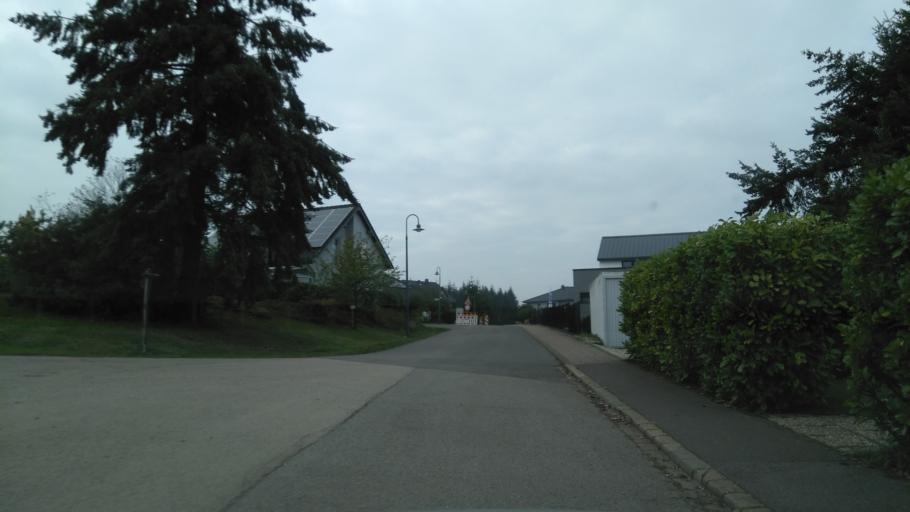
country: DE
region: Rheinland-Pfalz
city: Pellingen
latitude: 49.6758
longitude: 6.6668
